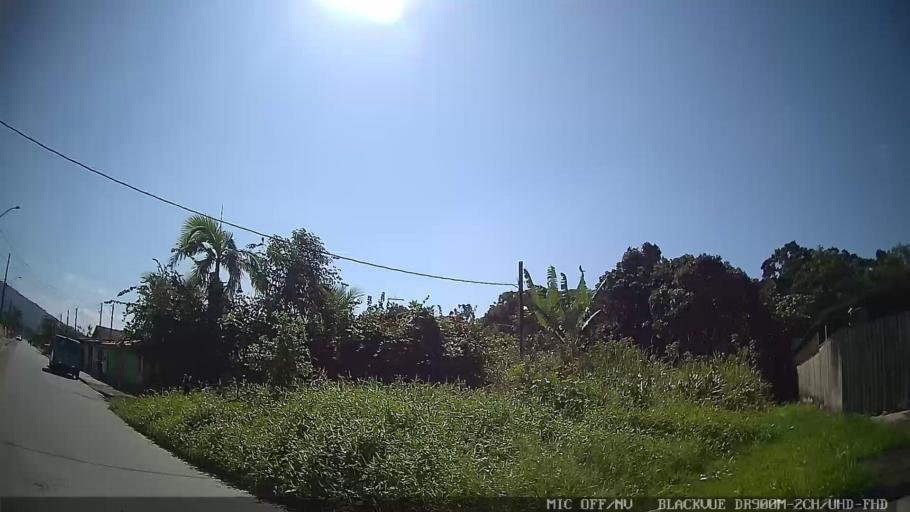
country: BR
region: Sao Paulo
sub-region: Itanhaem
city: Itanhaem
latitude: -24.1405
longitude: -46.7175
